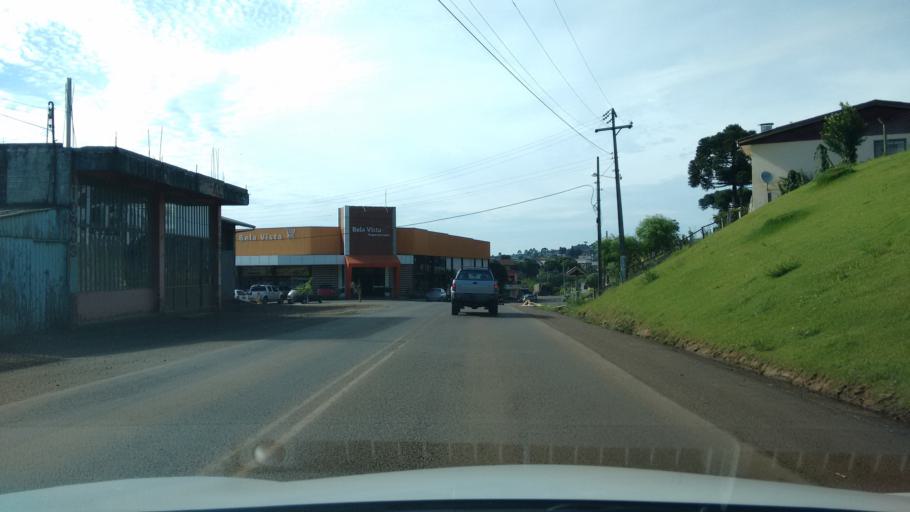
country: BR
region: Santa Catarina
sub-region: Videira
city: Videira
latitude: -27.2170
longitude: -50.9816
